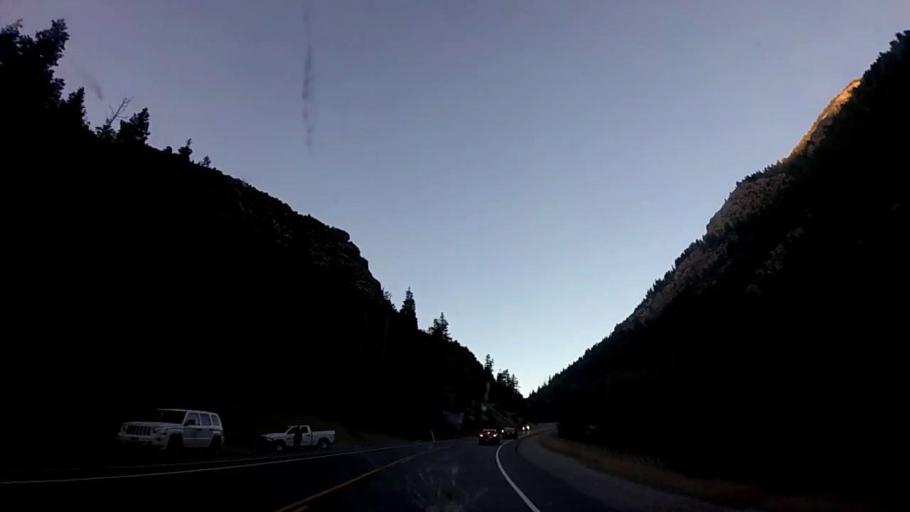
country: US
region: Utah
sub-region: Salt Lake County
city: Mount Olympus
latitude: 40.6364
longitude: -111.6998
